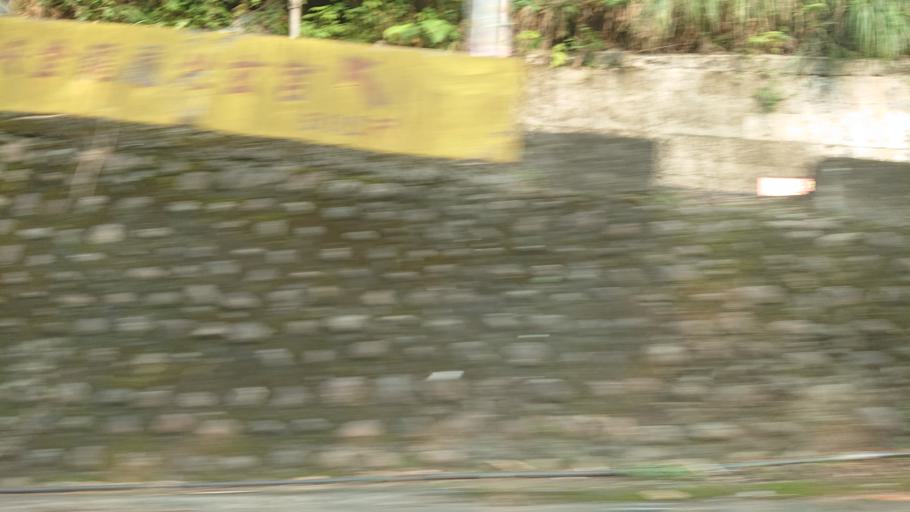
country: TW
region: Taiwan
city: Daxi
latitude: 24.8735
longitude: 121.3893
